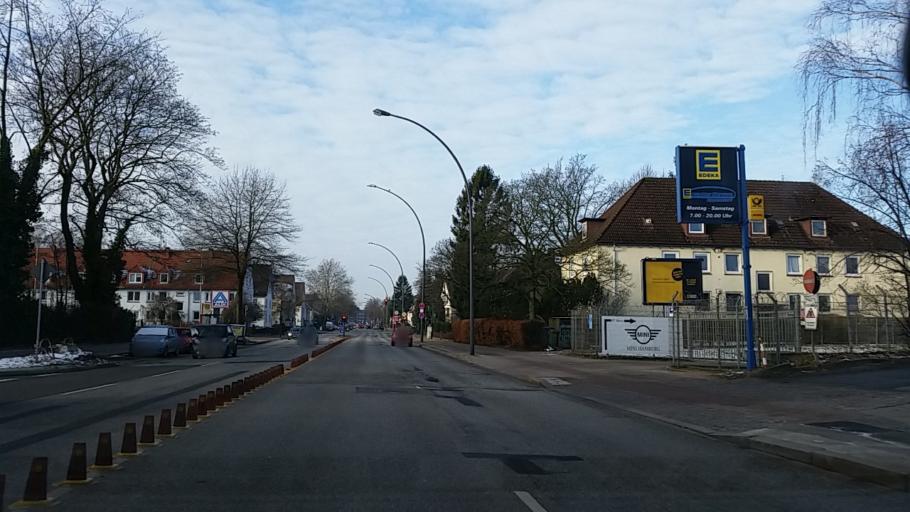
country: DE
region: Hamburg
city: Hamburg-Nord
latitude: 53.5984
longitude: 9.9736
